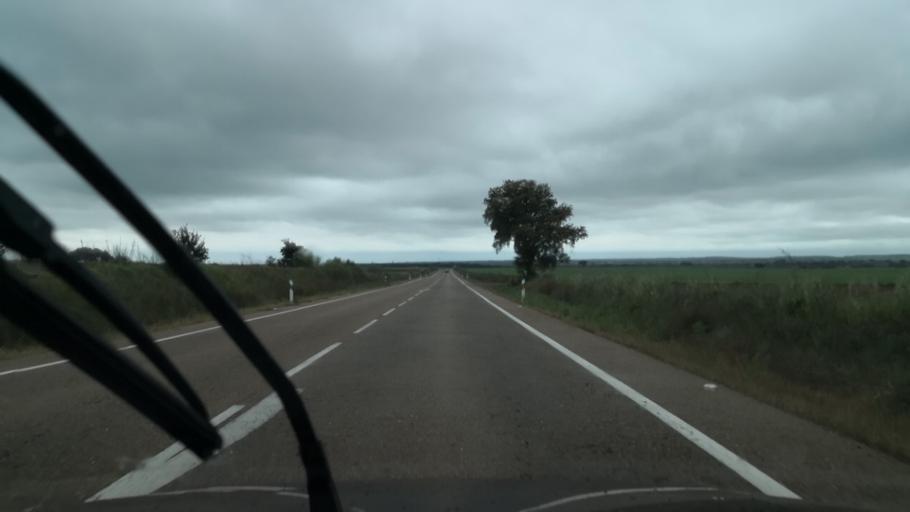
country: ES
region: Extremadura
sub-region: Provincia de Badajoz
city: Villar del Rey
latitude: 39.0562
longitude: -6.7913
